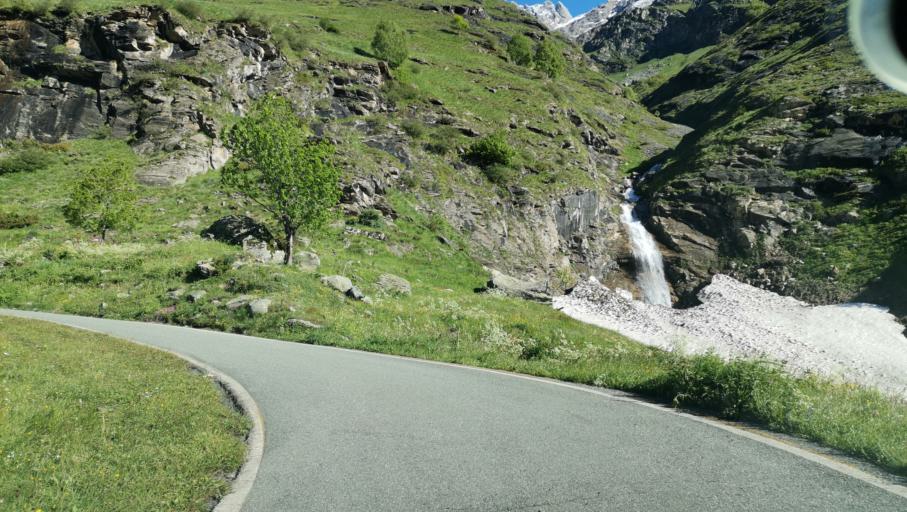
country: IT
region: Piedmont
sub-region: Provincia di Torino
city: Usseglio
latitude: 45.2096
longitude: 7.1634
